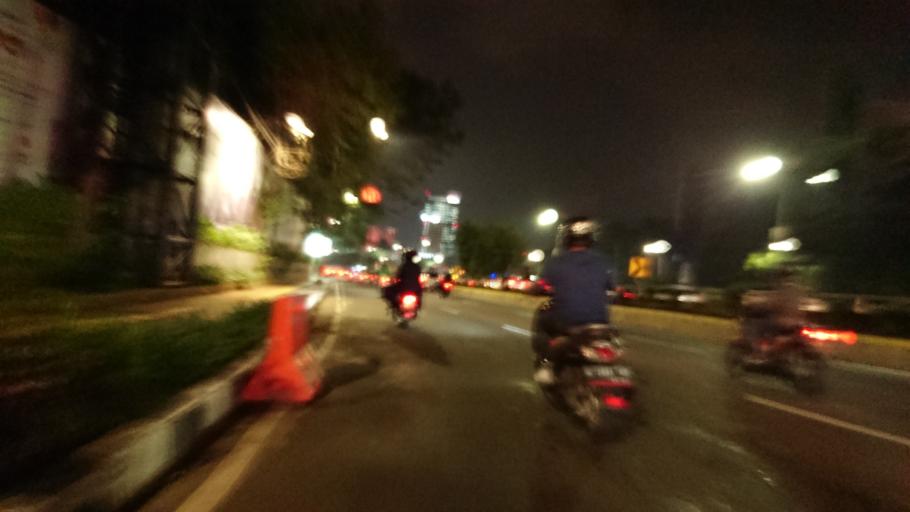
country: ID
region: Jakarta Raya
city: Jakarta
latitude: -6.2121
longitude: 106.8065
